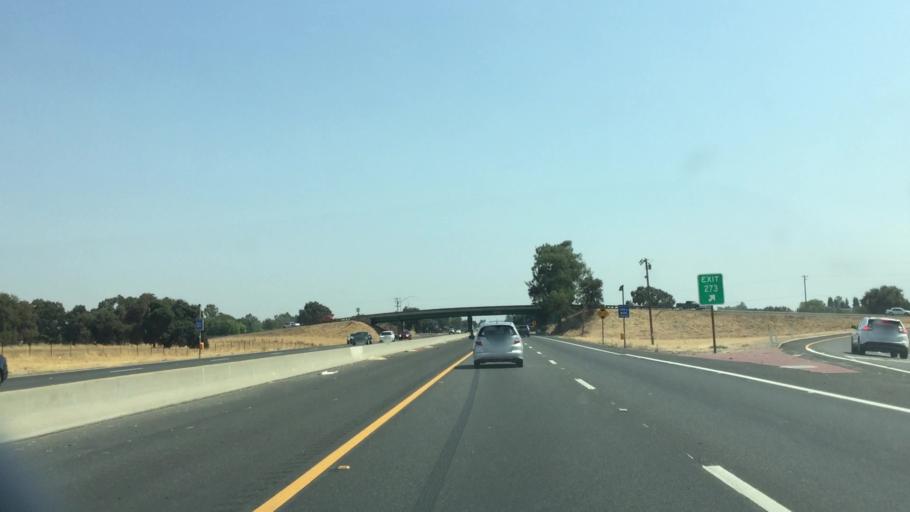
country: US
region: California
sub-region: San Joaquin County
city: Collierville
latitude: 38.2349
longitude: -121.2813
